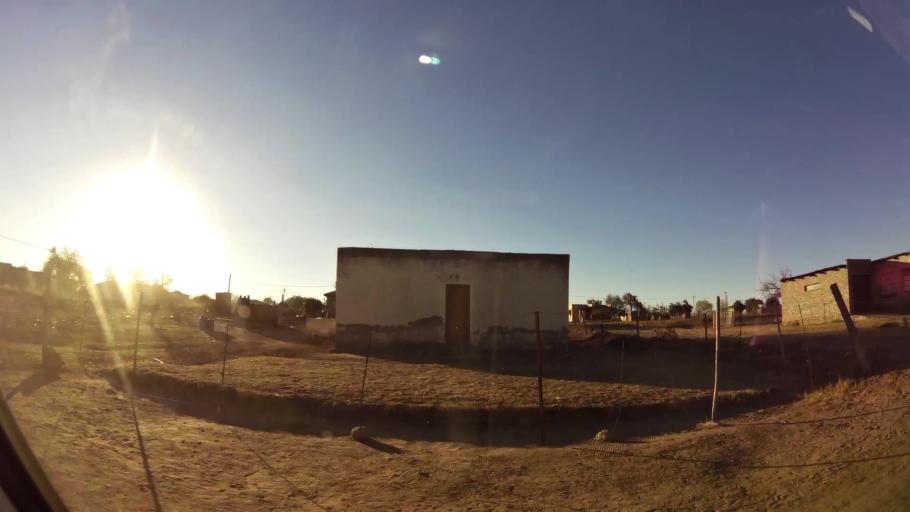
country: ZA
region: Limpopo
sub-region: Capricorn District Municipality
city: Polokwane
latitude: -23.8245
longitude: 29.3776
